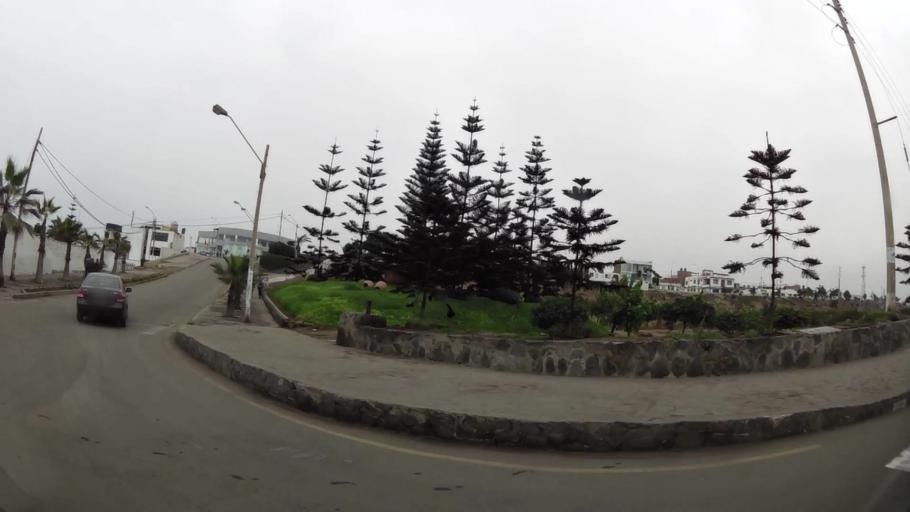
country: PE
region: Lima
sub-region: Lima
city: Punta Hermosa
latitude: -12.3370
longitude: -76.8248
